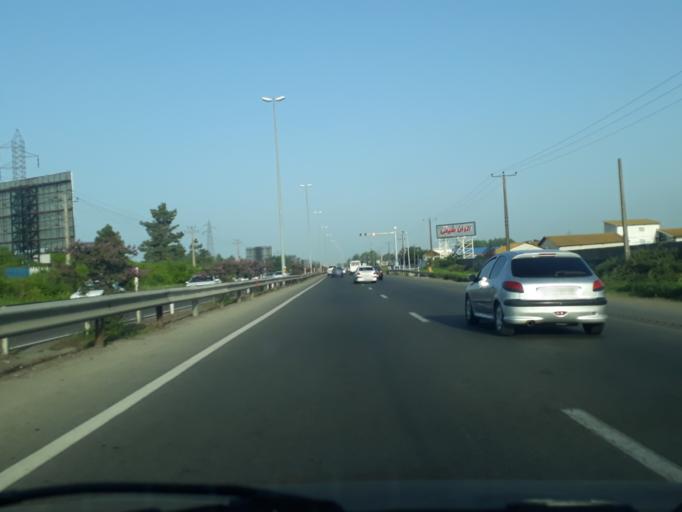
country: IR
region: Gilan
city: Bandar-e Anzali
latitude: 37.4593
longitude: 49.5952
